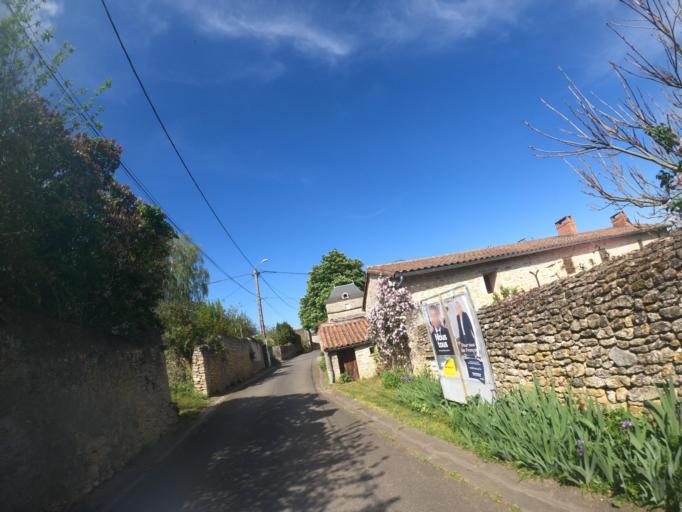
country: FR
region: Poitou-Charentes
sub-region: Departement des Deux-Sevres
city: Saint-Varent
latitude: 46.9107
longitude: -0.2136
